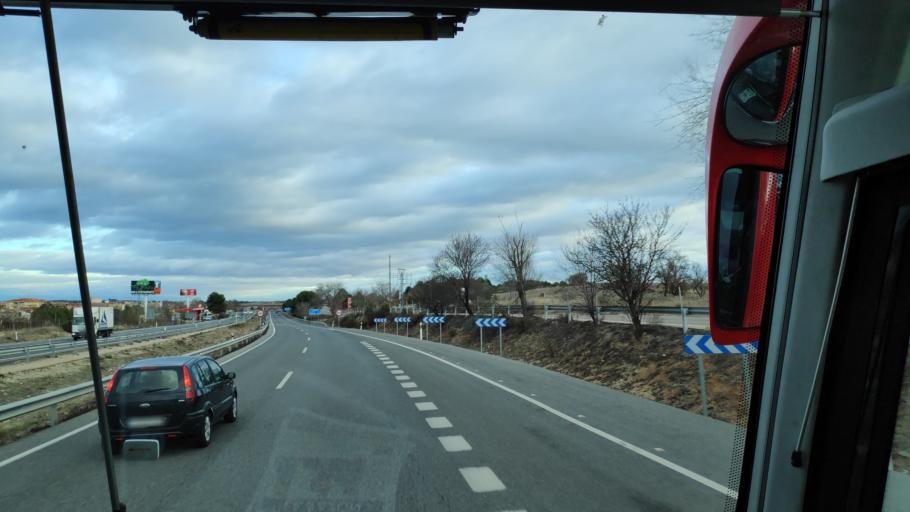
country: ES
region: Madrid
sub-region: Provincia de Madrid
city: Villarejo de Salvanes
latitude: 40.1693
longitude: -3.2894
